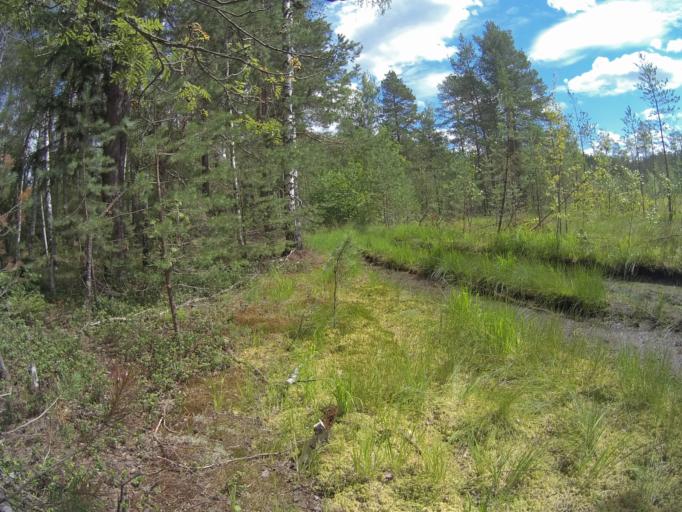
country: RU
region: Vladimir
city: Kommunar
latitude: 56.0553
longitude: 40.5184
